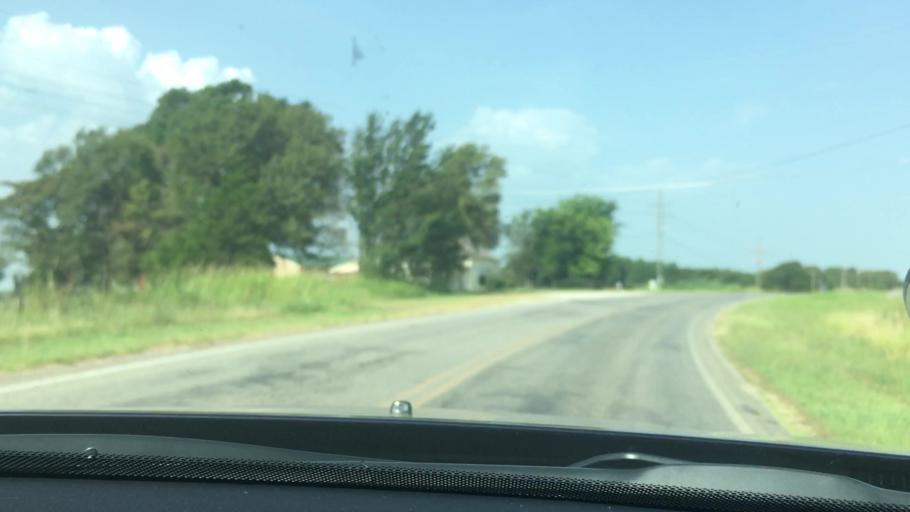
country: US
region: Oklahoma
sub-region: Pontotoc County
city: Byng
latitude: 34.8650
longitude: -96.6010
